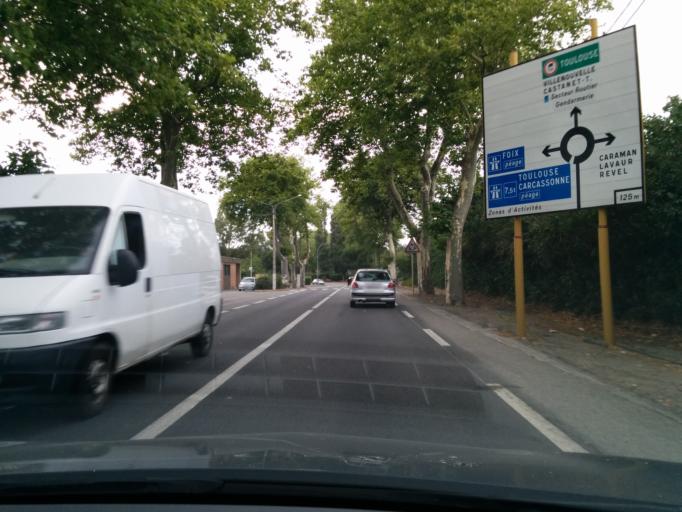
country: FR
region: Midi-Pyrenees
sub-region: Departement de la Haute-Garonne
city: Villefranche-de-Lauragais
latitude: 43.4047
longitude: 1.7104
